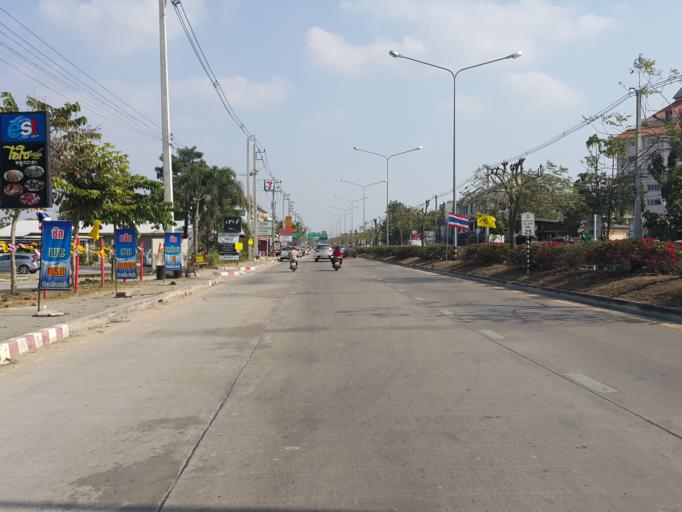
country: TH
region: Chiang Mai
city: Chiang Mai
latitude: 18.7472
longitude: 98.9516
